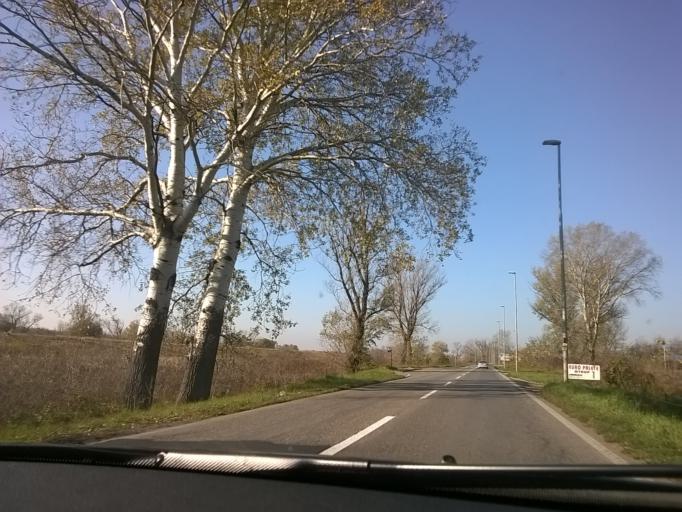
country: RS
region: Autonomna Pokrajina Vojvodina
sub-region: Juznobanatski Okrug
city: Pancevo
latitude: 44.8698
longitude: 20.6076
